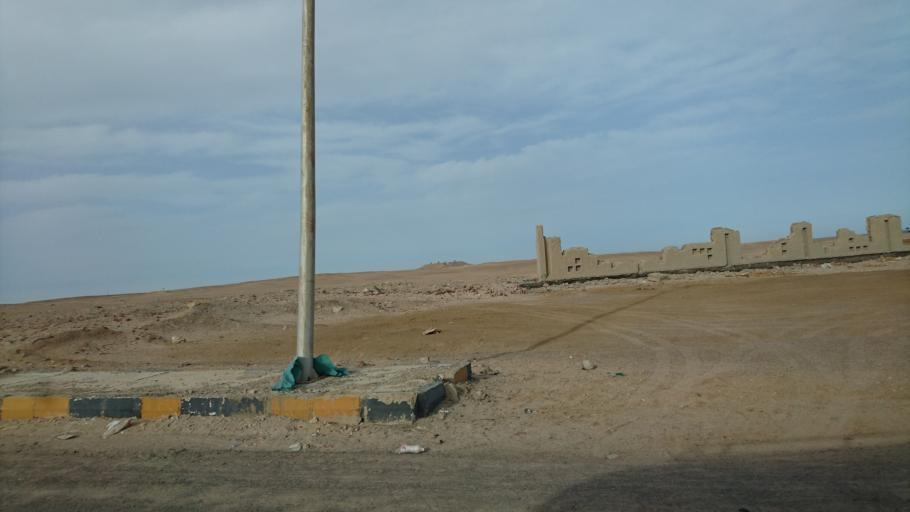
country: EG
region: Red Sea
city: Bur Safajah
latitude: 26.8022
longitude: 33.9379
